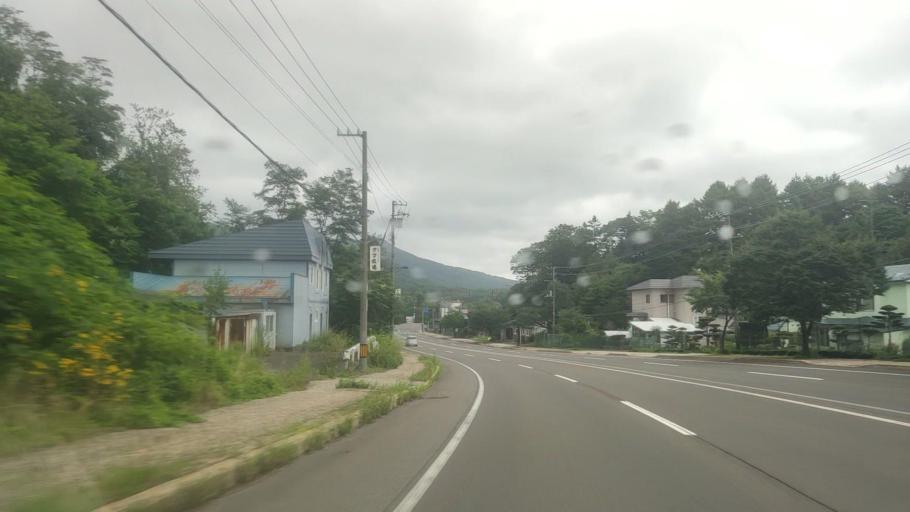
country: JP
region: Hokkaido
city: Shiraoi
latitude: 42.4702
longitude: 141.1537
